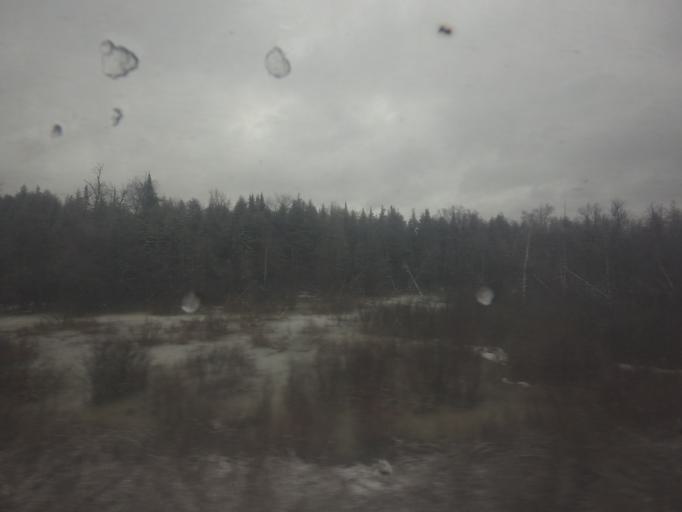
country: CA
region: Ontario
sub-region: Lanark County
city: Smiths Falls
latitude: 44.9450
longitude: -76.0175
